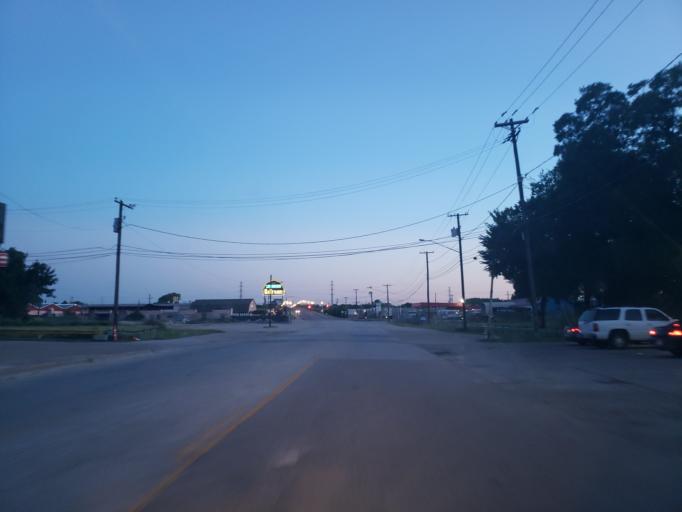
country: US
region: Texas
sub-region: Dallas County
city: Dallas
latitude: 32.7617
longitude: -96.7929
